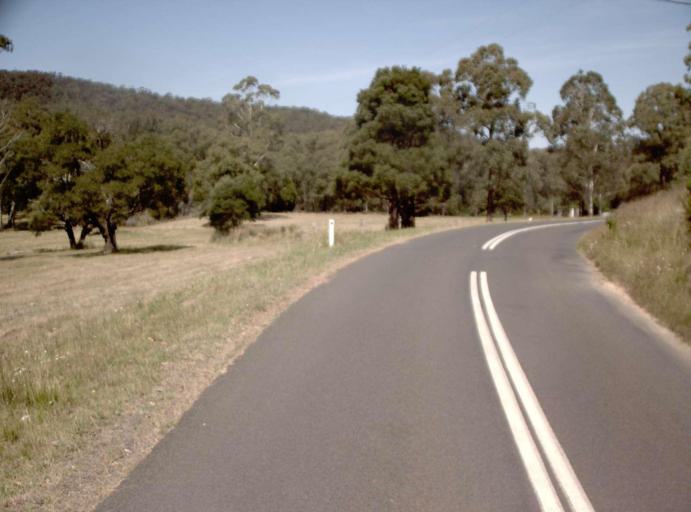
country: AU
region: Victoria
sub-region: Baw Baw
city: Warragul
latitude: -37.8964
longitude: 146.0068
